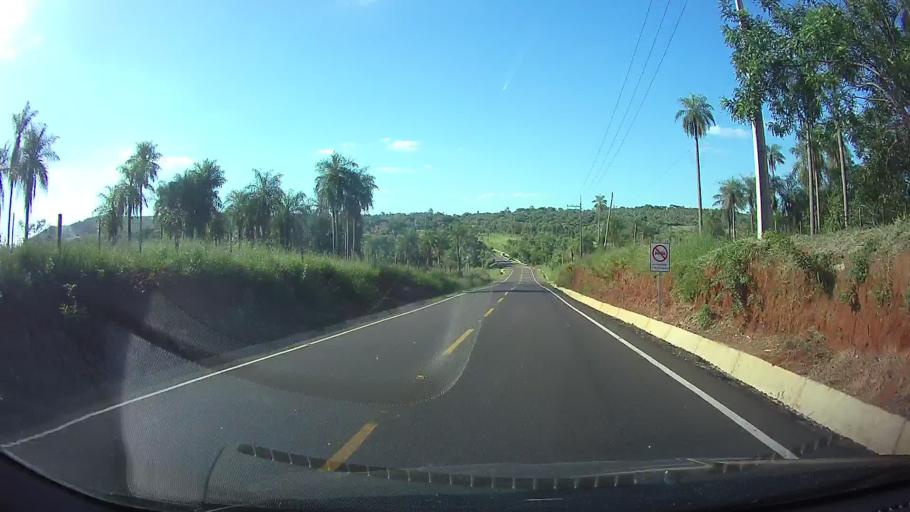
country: PY
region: Cordillera
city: Caacupe
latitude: -25.3566
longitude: -57.1473
